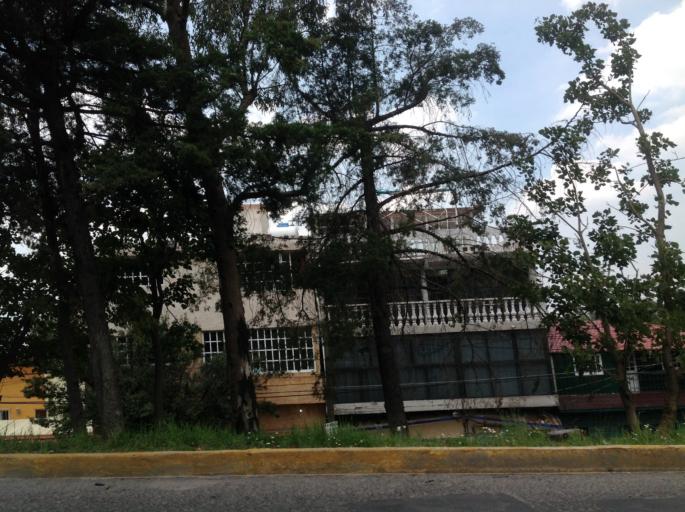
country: MX
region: Mexico
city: Ciudad Lopez Mateos
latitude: 19.5965
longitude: -99.2283
